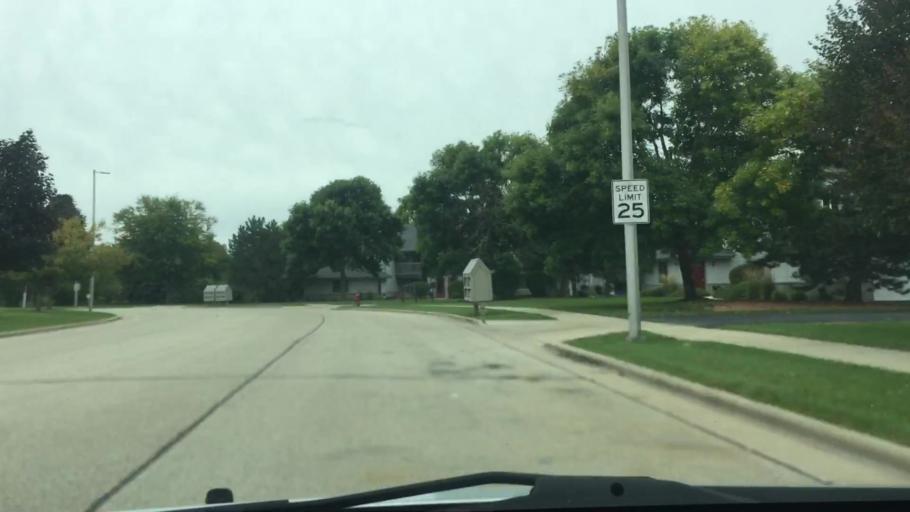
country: US
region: Wisconsin
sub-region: Waukesha County
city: Pewaukee
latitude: 43.0924
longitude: -88.2785
